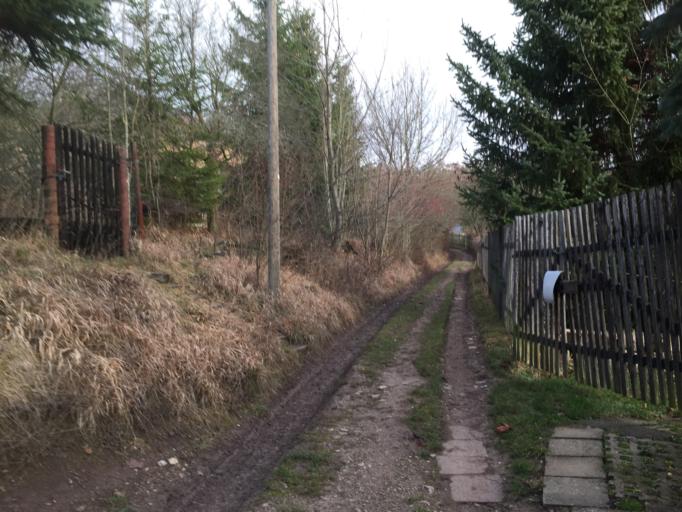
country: DE
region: Thuringia
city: Bad Blankenburg
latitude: 50.6870
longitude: 11.2647
